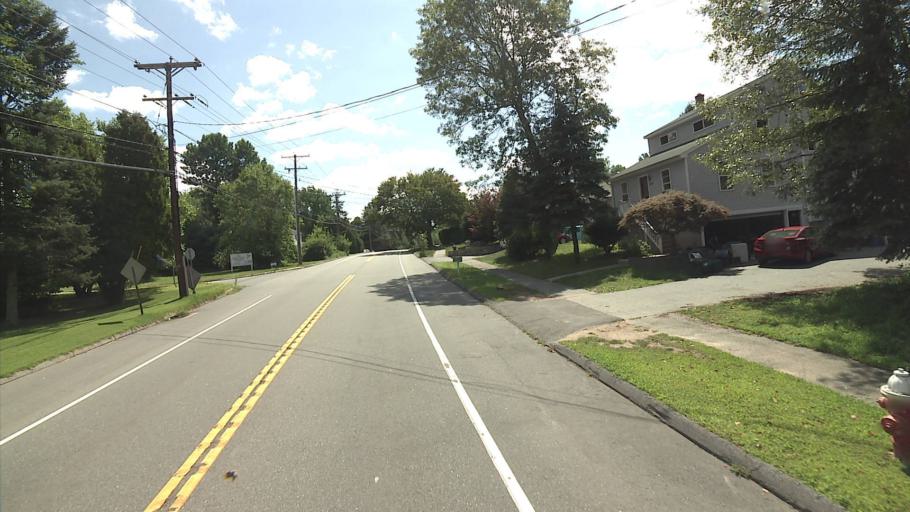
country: US
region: Connecticut
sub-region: New London County
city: Niantic
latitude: 41.3680
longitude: -72.1861
